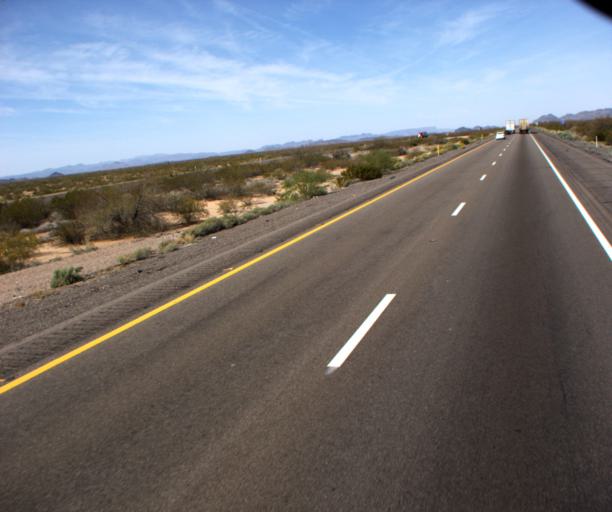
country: US
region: Arizona
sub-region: La Paz County
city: Salome
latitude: 33.5889
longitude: -113.4828
